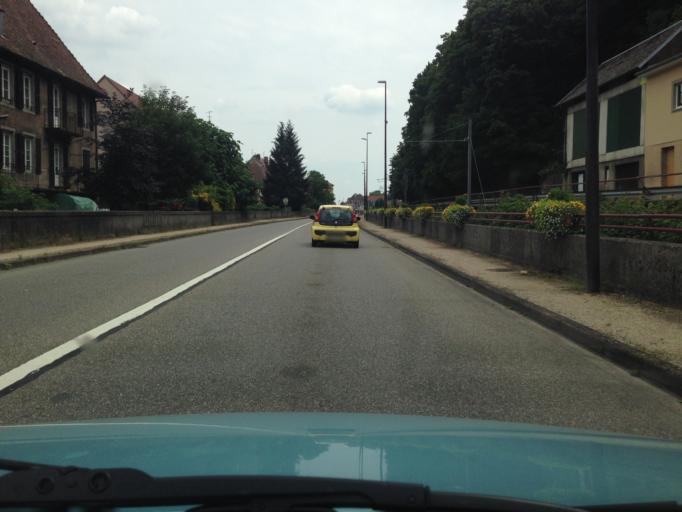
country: FR
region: Alsace
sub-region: Departement du Haut-Rhin
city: Thann
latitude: 47.8116
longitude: 7.0977
